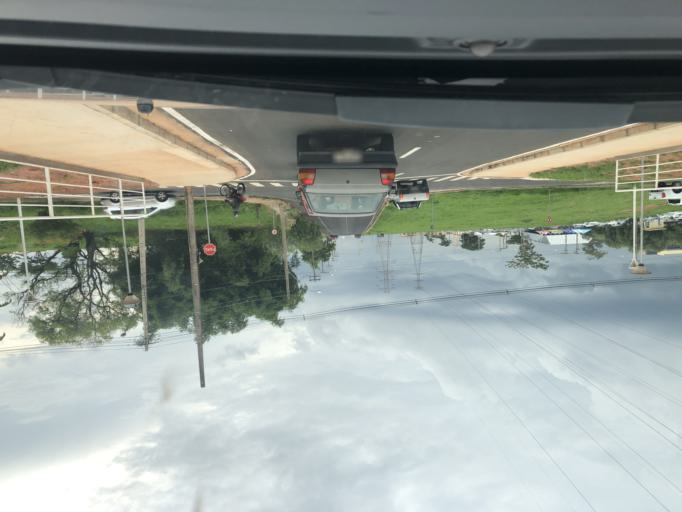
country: BR
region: Sao Paulo
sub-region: Sao Jose Do Rio Preto
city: Sao Jose do Rio Preto
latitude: -20.8424
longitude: -49.4116
